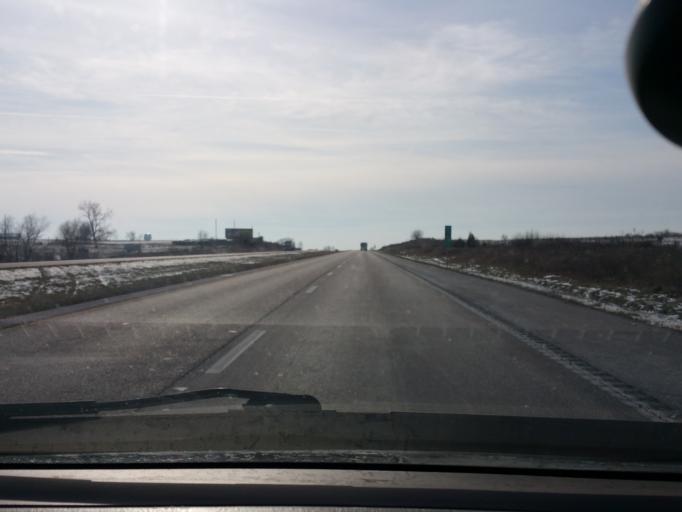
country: US
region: Missouri
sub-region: Clinton County
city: Lathrop
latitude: 39.5273
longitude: -94.2799
